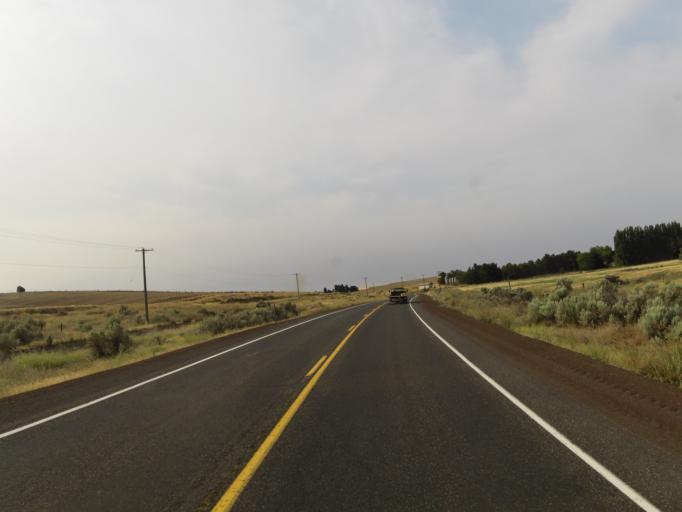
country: US
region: Oregon
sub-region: Sherman County
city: Moro
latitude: 45.4560
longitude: -120.7497
